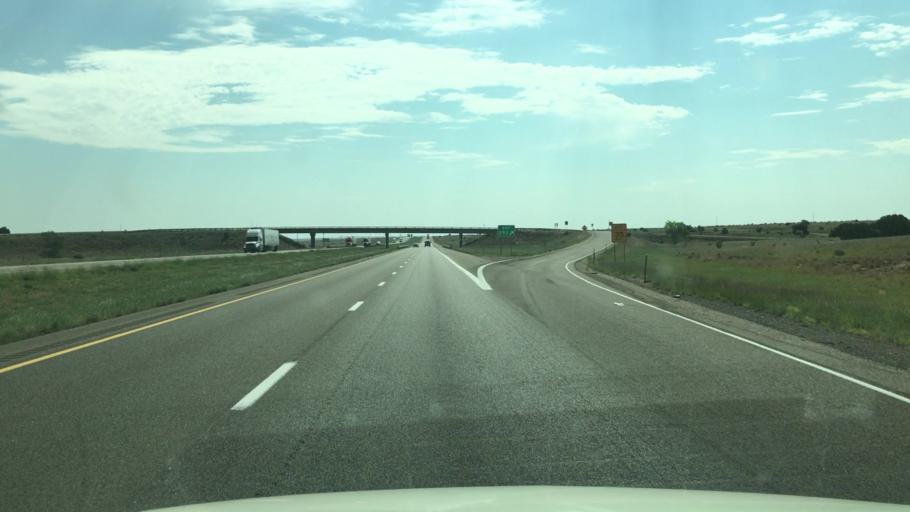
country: US
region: New Mexico
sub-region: Guadalupe County
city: Santa Rosa
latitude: 34.9803
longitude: -105.0699
